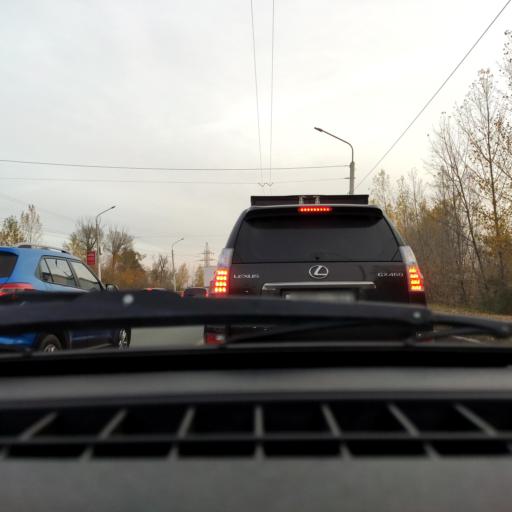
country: RU
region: Bashkortostan
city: Ufa
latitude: 54.7886
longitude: 56.0779
